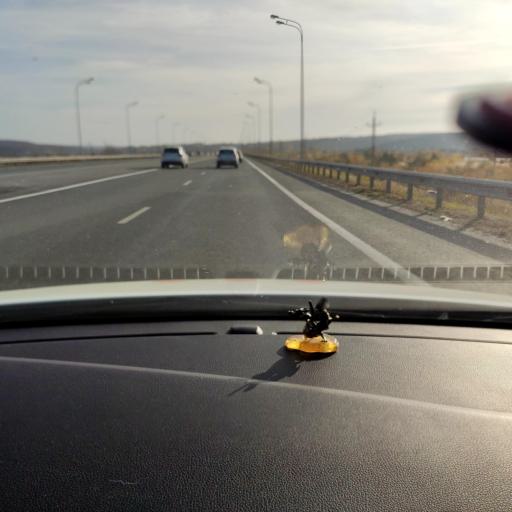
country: RU
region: Tatarstan
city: Osinovo
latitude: 55.8040
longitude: 48.8414
